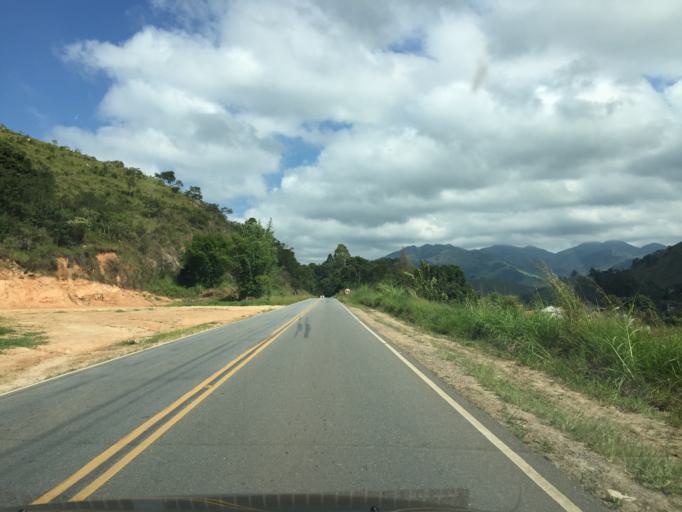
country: BR
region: Minas Gerais
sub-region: Passa Quatro
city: Passa Quatro
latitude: -22.3763
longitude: -44.9628
